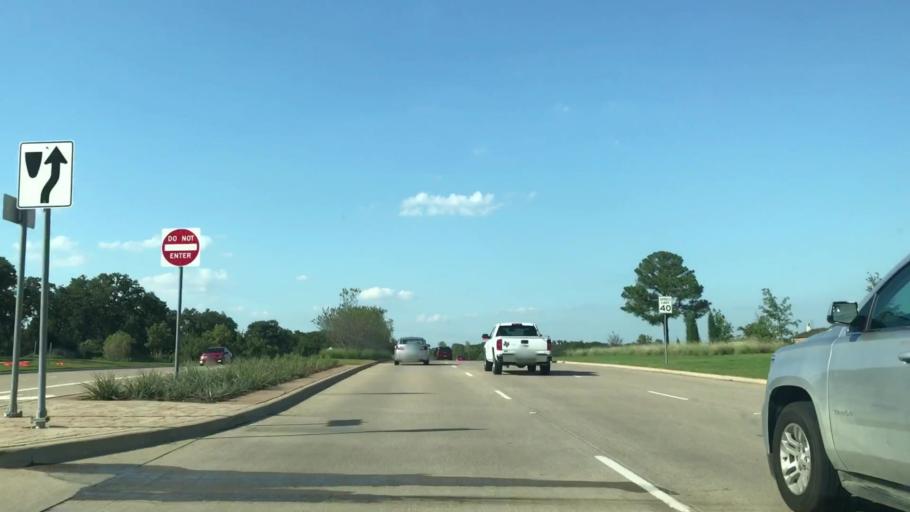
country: US
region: Texas
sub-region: Denton County
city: Trophy Club
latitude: 32.9813
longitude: -97.1853
